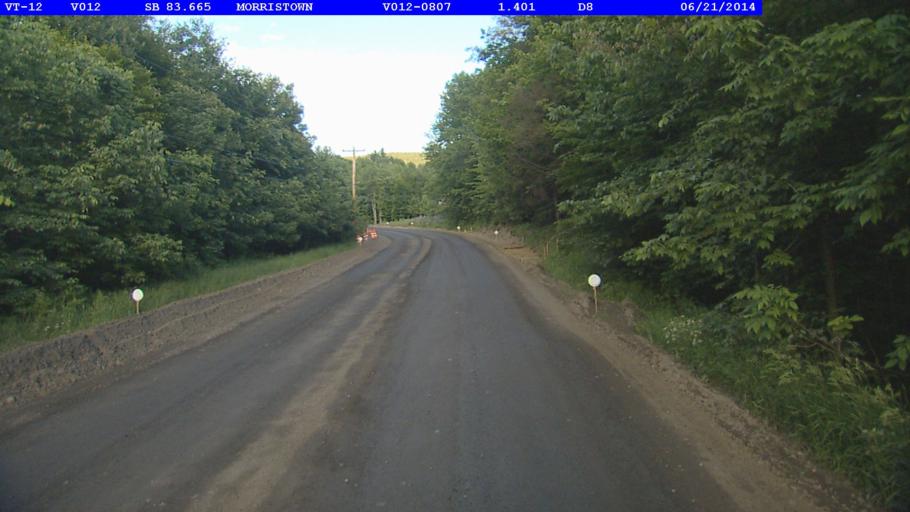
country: US
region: Vermont
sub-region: Lamoille County
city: Morrisville
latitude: 44.5479
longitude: -72.5650
